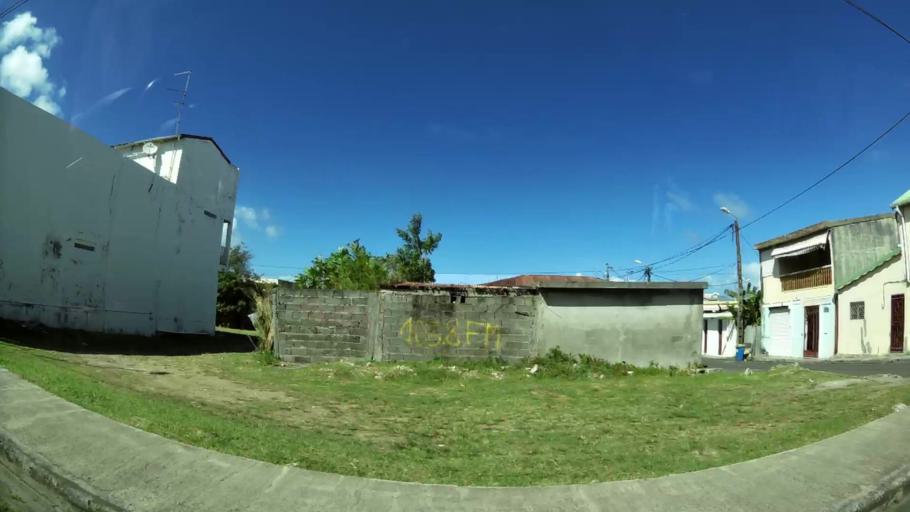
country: GP
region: Guadeloupe
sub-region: Guadeloupe
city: Le Moule
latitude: 16.3305
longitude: -61.3496
